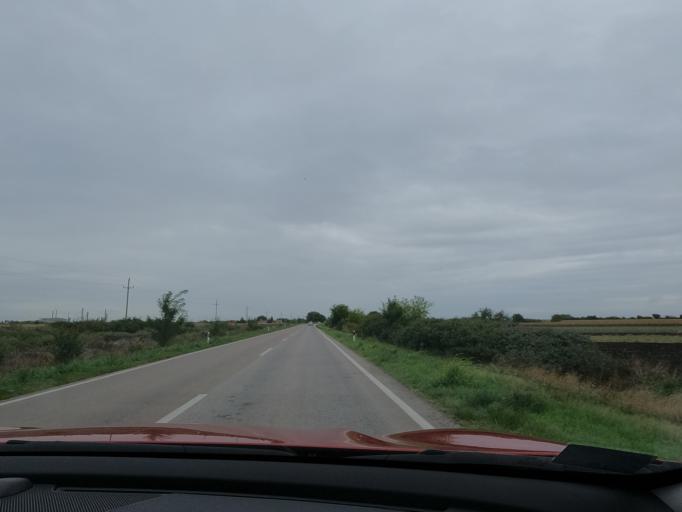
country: RS
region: Autonomna Pokrajina Vojvodina
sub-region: Severnobanatski Okrug
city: Kikinda
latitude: 45.7770
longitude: 20.4276
